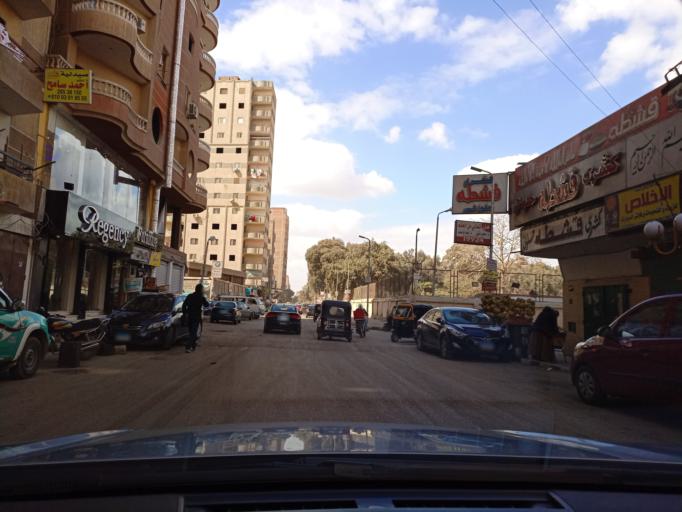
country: EG
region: Muhafazat al Qalyubiyah
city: Al Khankah
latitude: 30.1223
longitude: 31.3426
